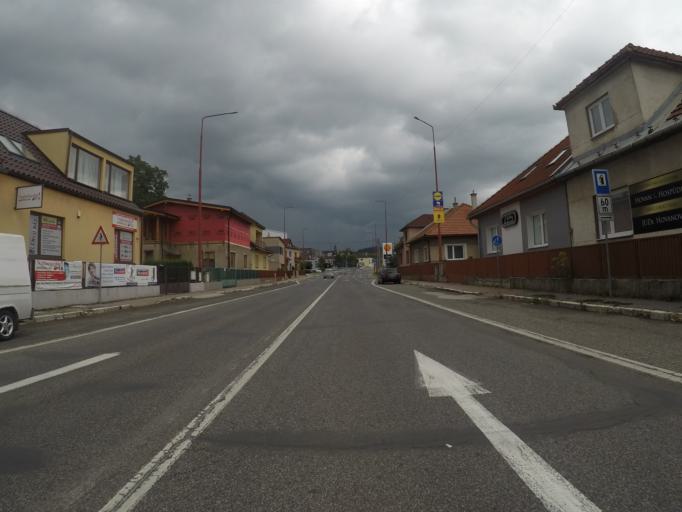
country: SK
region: Kosicky
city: Spisska Nova Ves
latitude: 48.9412
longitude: 20.5598
